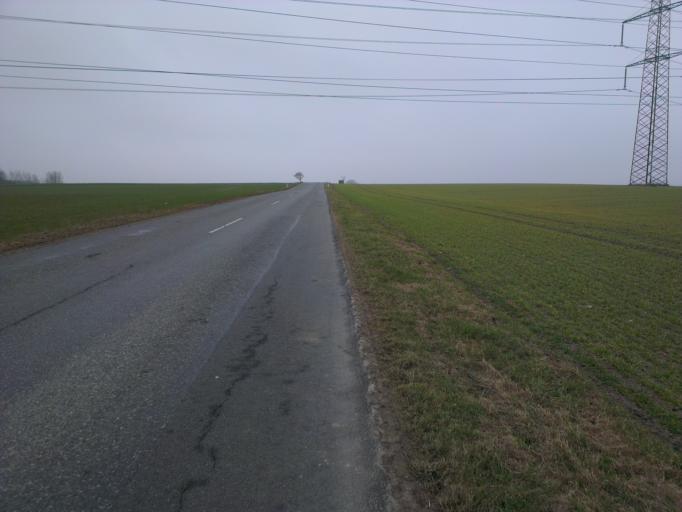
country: DK
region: Capital Region
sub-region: Frederikssund Kommune
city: Frederikssund
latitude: 55.7990
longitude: 12.0185
